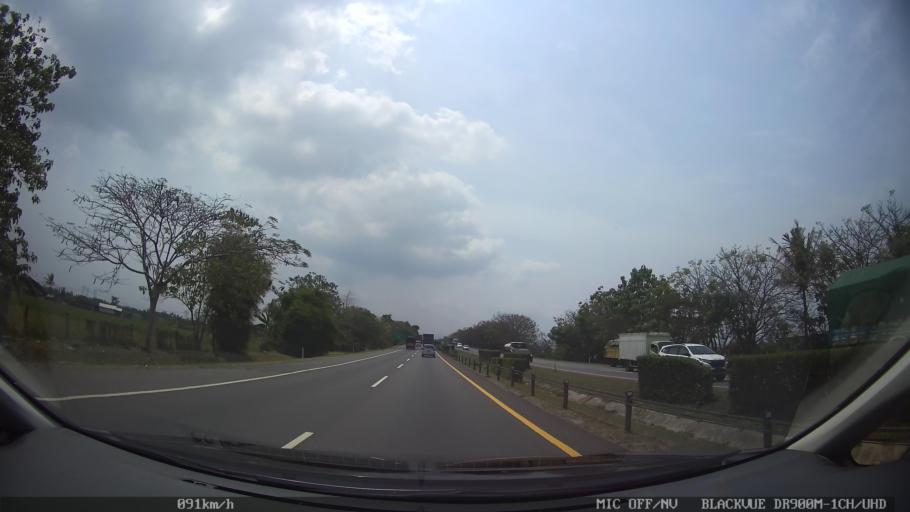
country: ID
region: Banten
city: Bojonegara
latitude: -6.0330
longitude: 106.1005
